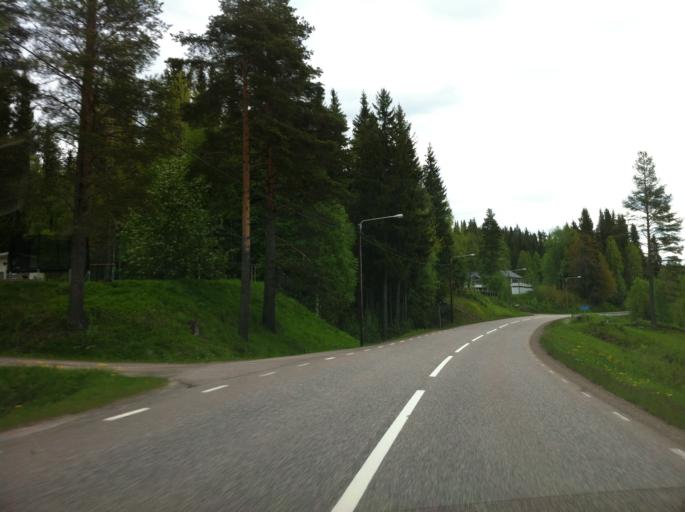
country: SE
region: Dalarna
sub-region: Malung-Saelens kommun
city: Malung
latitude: 61.1313
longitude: 13.2834
